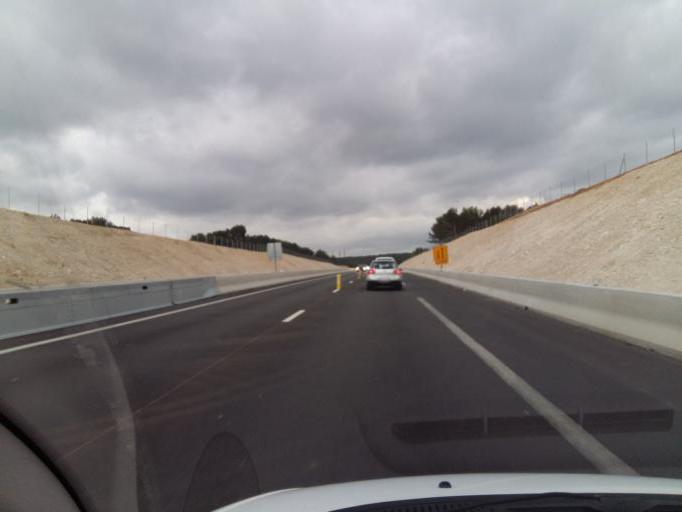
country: FR
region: Provence-Alpes-Cote d'Azur
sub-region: Departement des Bouches-du-Rhone
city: Cabries
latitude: 43.4708
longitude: 5.3421
